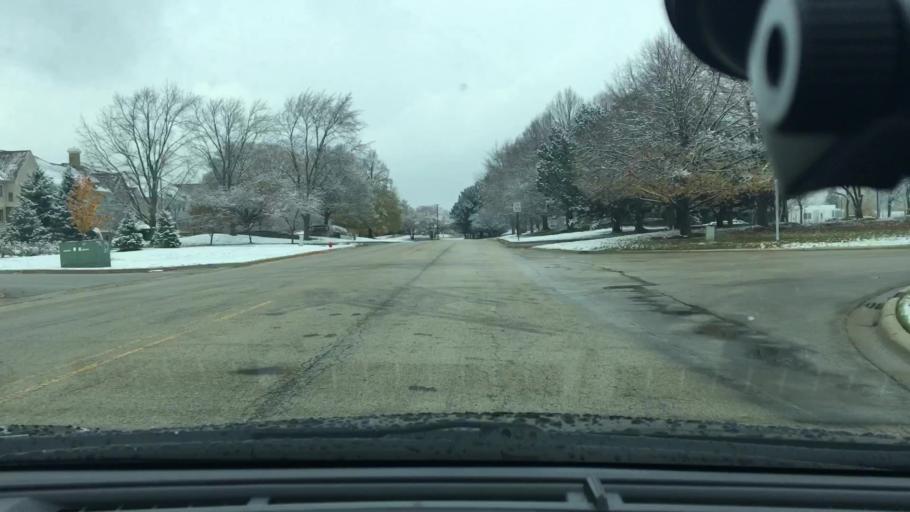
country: US
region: Illinois
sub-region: Lake County
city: Lincolnshire
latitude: 42.1946
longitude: -87.9368
